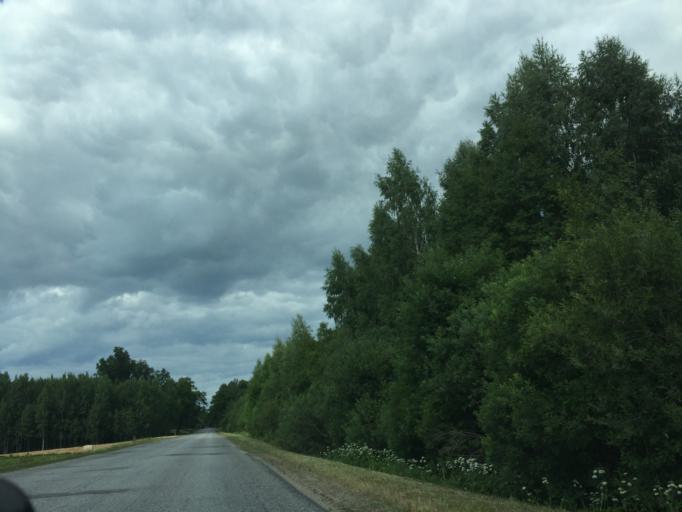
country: LV
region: Skriveri
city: Skriveri
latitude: 56.8269
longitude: 25.1251
